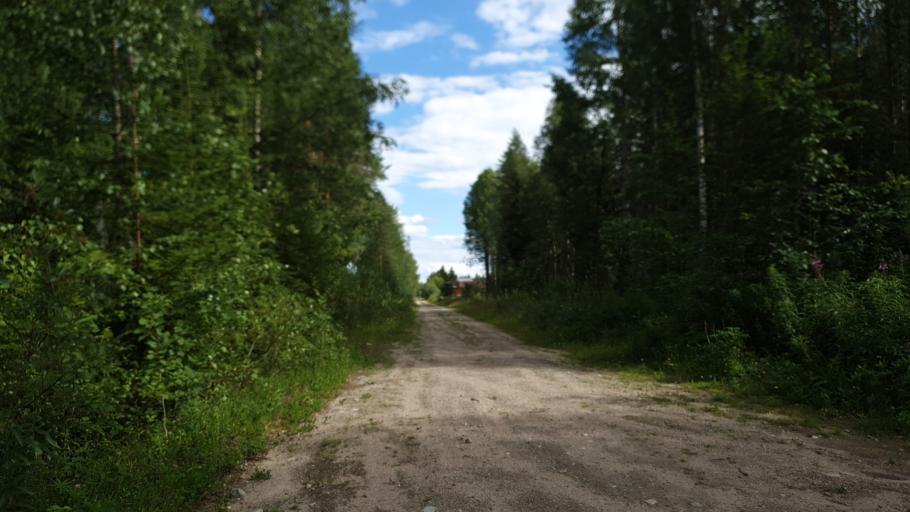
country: FI
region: Kainuu
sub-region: Kehys-Kainuu
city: Kuhmo
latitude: 64.1143
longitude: 29.5191
